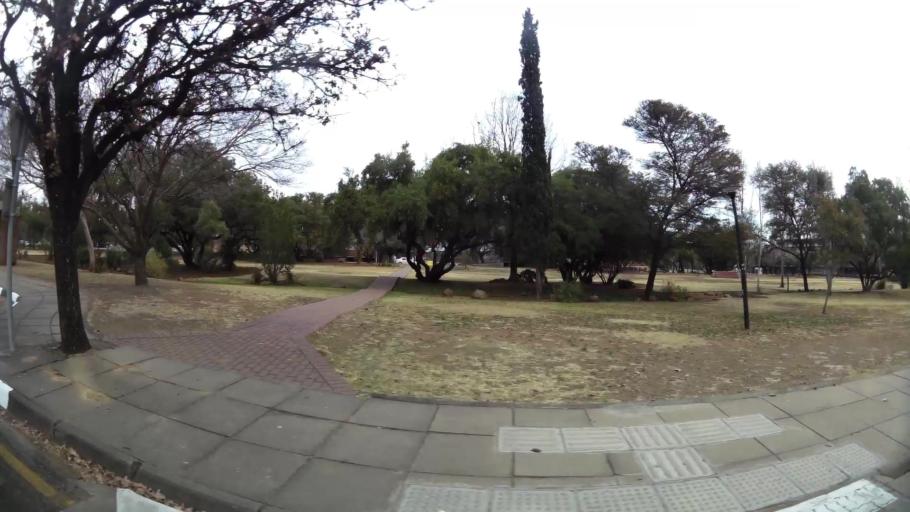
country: ZA
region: Orange Free State
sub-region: Mangaung Metropolitan Municipality
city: Bloemfontein
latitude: -29.1090
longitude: 26.1919
